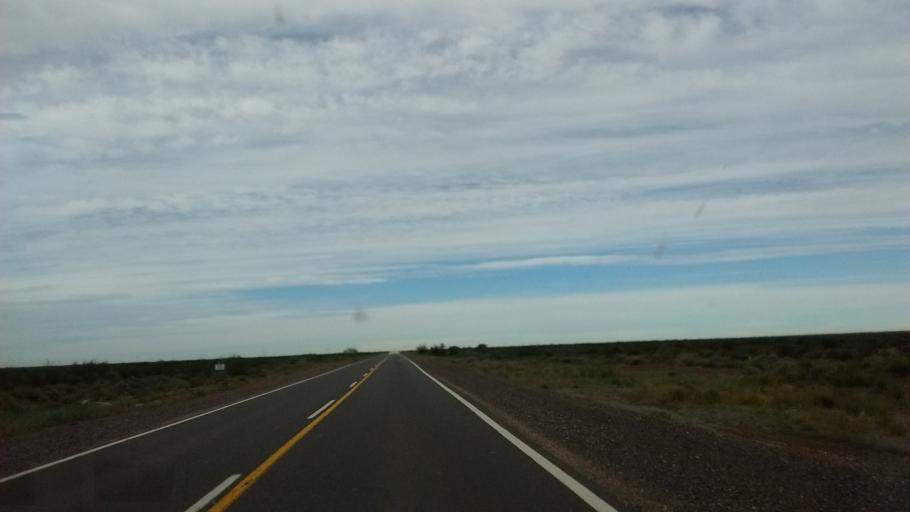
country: AR
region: Rio Negro
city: Contraalmirante Cordero
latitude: -38.5278
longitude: -68.0763
